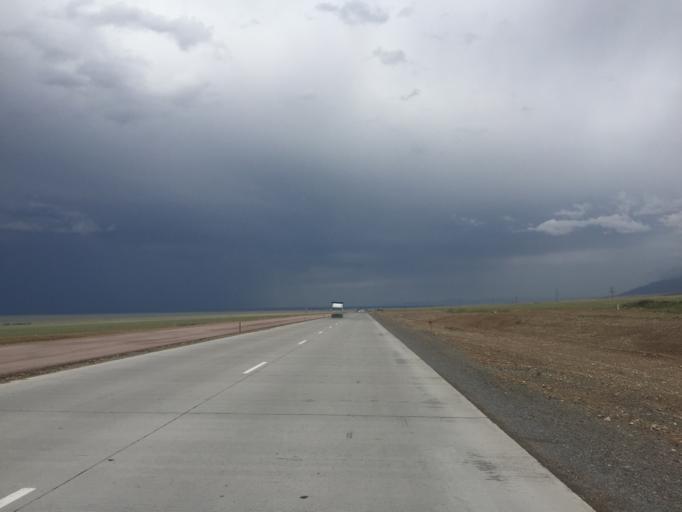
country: KG
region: Chuy
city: Ivanovka
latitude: 43.3818
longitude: 75.1942
